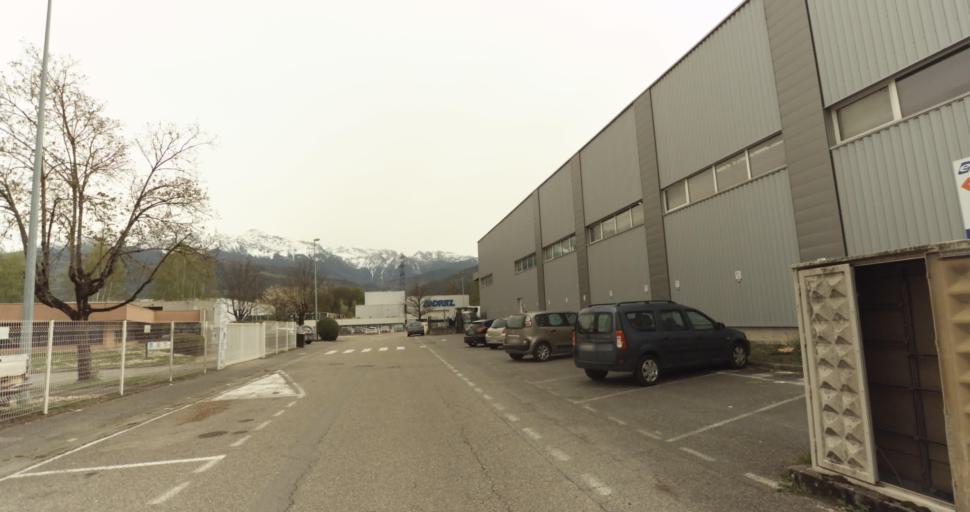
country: FR
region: Rhone-Alpes
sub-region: Departement de l'Isere
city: Montbonnot-Saint-Martin
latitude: 45.2213
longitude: 5.8171
